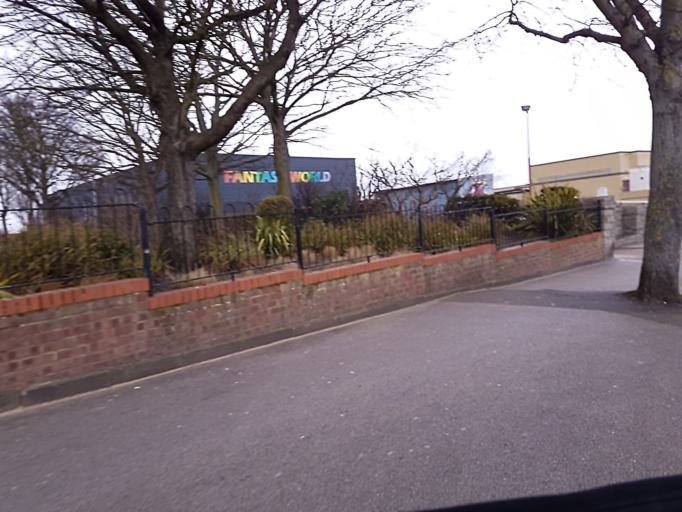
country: GB
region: England
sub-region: North East Lincolnshire
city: Cleethorpes
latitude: 53.5608
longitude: -0.0287
